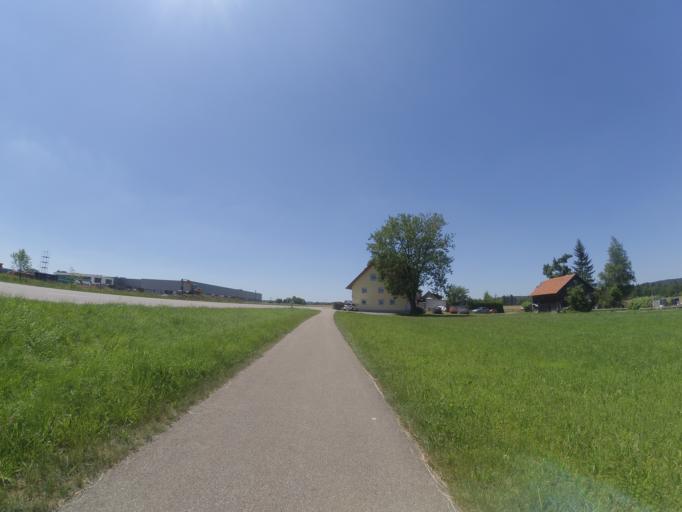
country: DE
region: Baden-Wuerttemberg
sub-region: Tuebingen Region
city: Bad Wurzach
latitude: 47.8997
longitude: 9.8627
